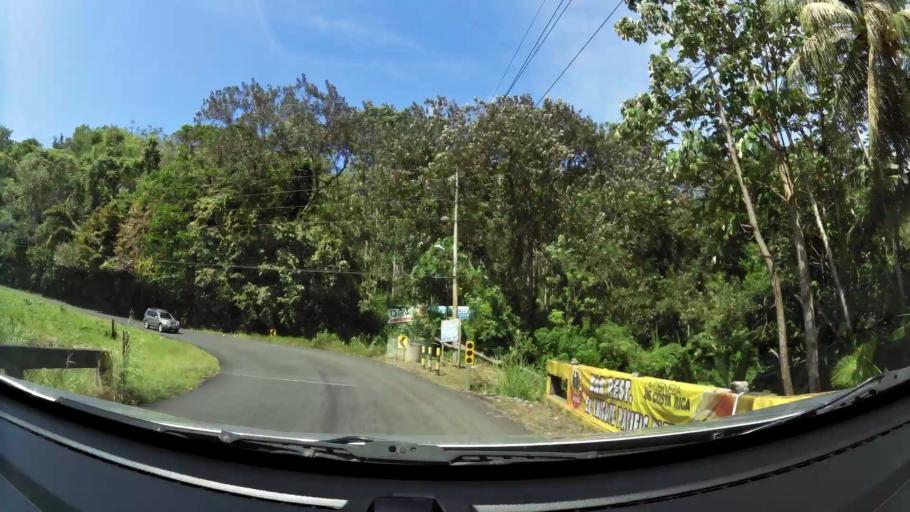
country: CR
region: San Jose
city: San Isidro
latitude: 9.2830
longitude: -83.8390
